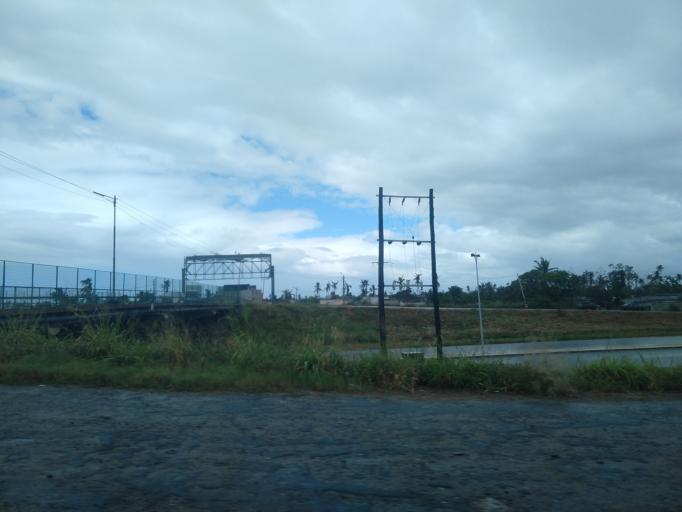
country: MZ
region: Sofala
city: Beira
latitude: -19.7826
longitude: 34.8778
